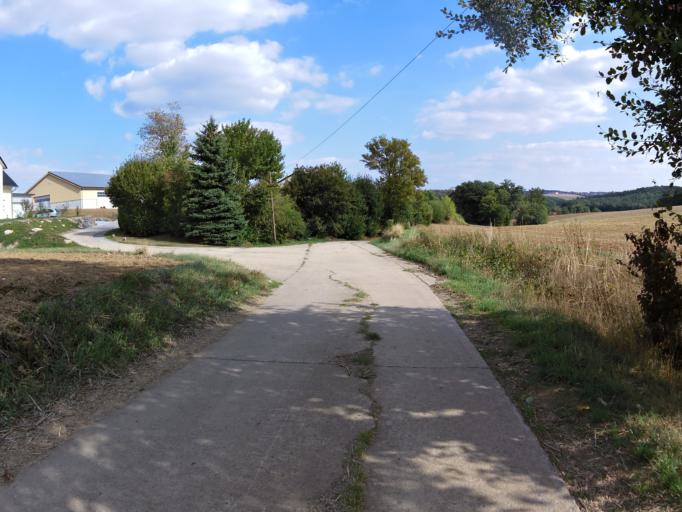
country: DE
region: Bavaria
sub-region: Regierungsbezirk Unterfranken
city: Hettstadt
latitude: 49.7849
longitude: 9.7957
